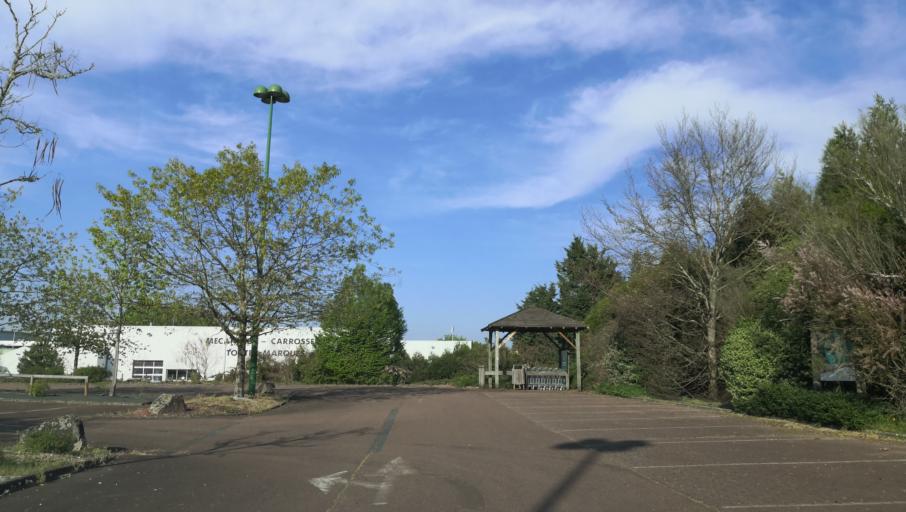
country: FR
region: Limousin
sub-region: Departement de la Haute-Vienne
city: Couzeix
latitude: 45.8658
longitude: 1.2684
